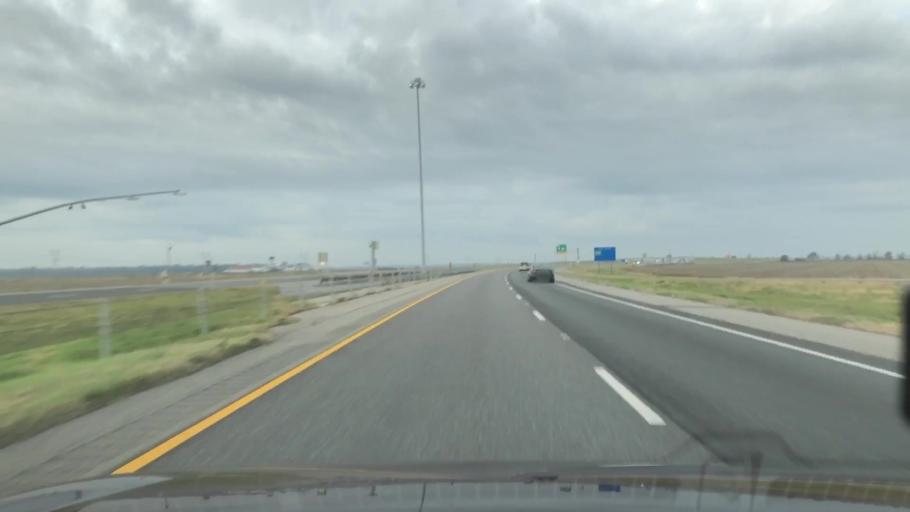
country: US
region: Mississippi
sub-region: Warren County
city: Vicksburg
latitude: 32.3199
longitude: -90.9490
